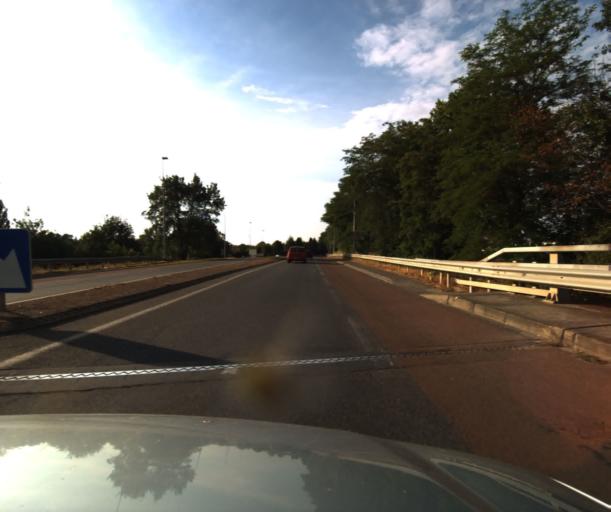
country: FR
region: Midi-Pyrenees
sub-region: Departement du Tarn-et-Garonne
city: Castelsarrasin
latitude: 44.0547
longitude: 1.1001
